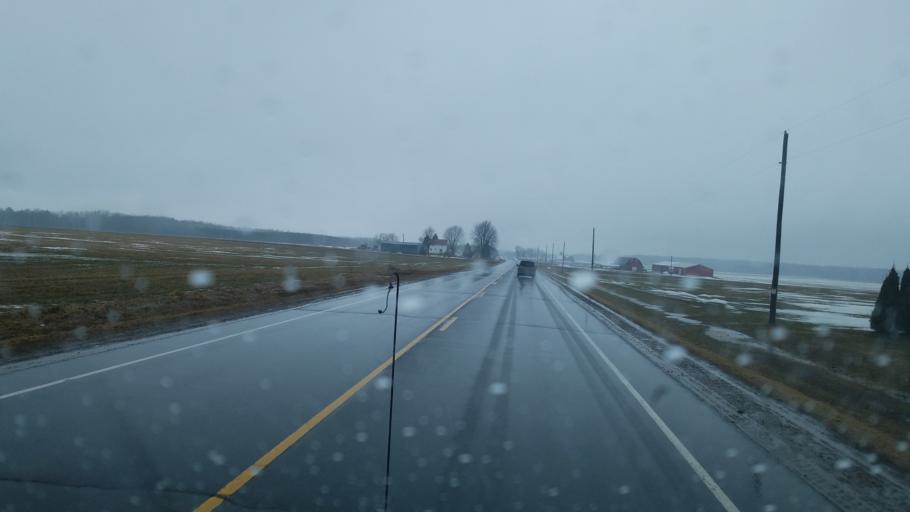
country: US
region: Wisconsin
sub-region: Marathon County
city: Spencer
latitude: 44.6562
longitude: -90.3330
